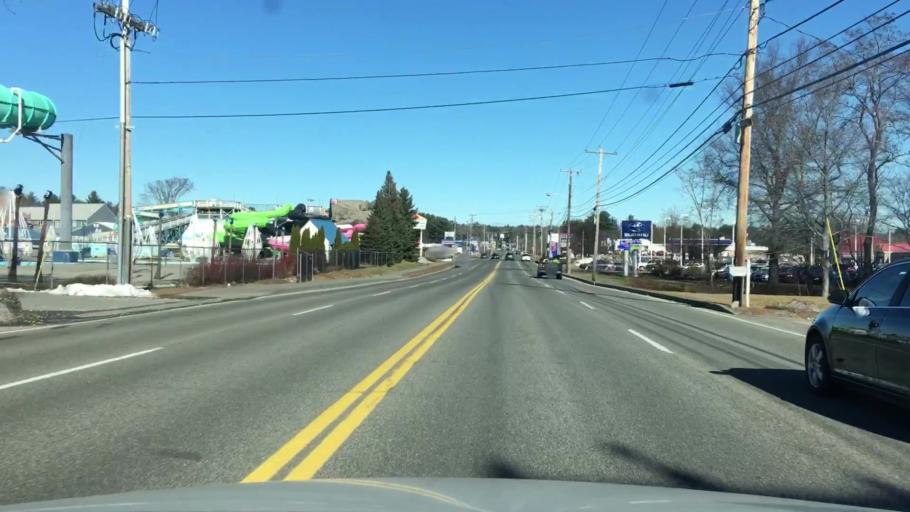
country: US
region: Maine
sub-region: York County
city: Saco
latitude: 43.5266
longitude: -70.4274
